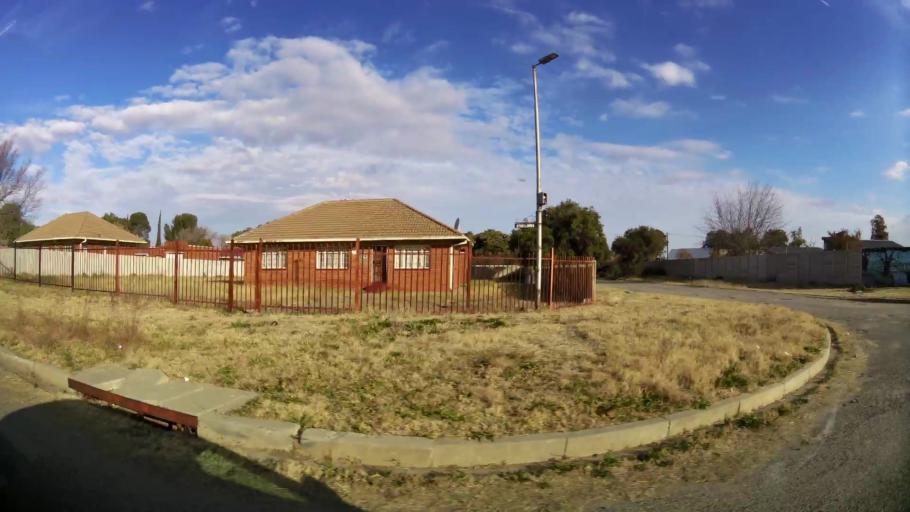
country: ZA
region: Orange Free State
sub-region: Lejweleputswa District Municipality
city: Welkom
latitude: -27.9873
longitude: 26.7067
